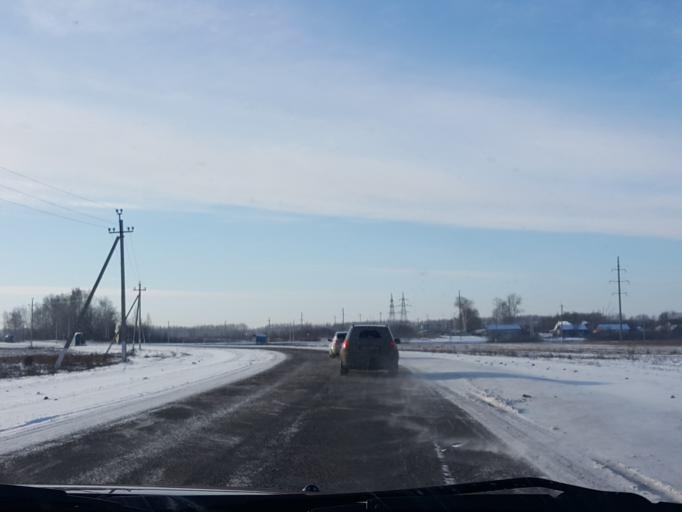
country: RU
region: Tambov
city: Znamenka
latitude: 52.4080
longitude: 41.4666
